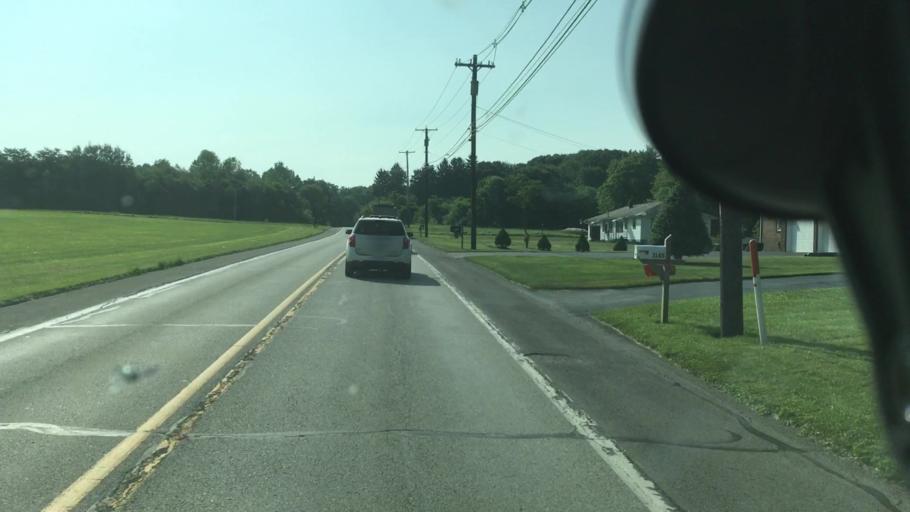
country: US
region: Pennsylvania
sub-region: Lawrence County
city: Oakwood
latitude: 41.0219
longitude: -80.4221
